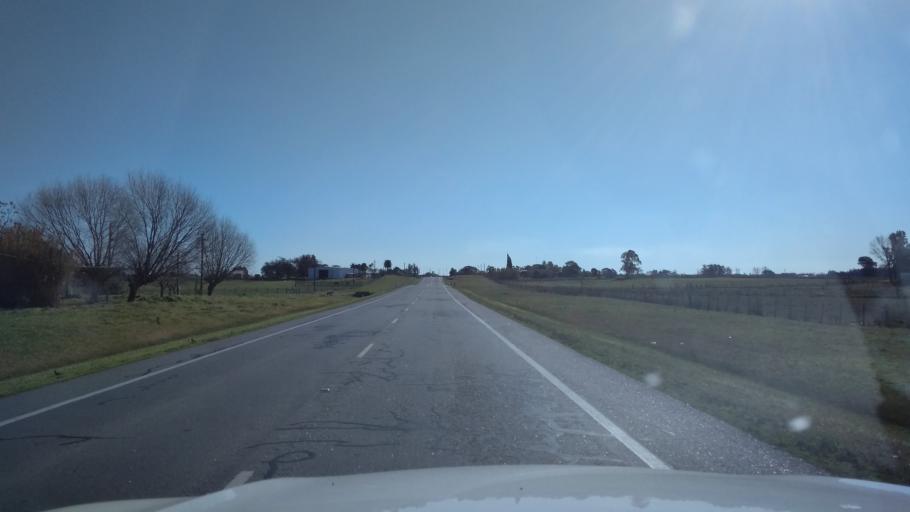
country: UY
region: Canelones
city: San Jacinto
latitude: -34.5325
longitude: -55.9411
